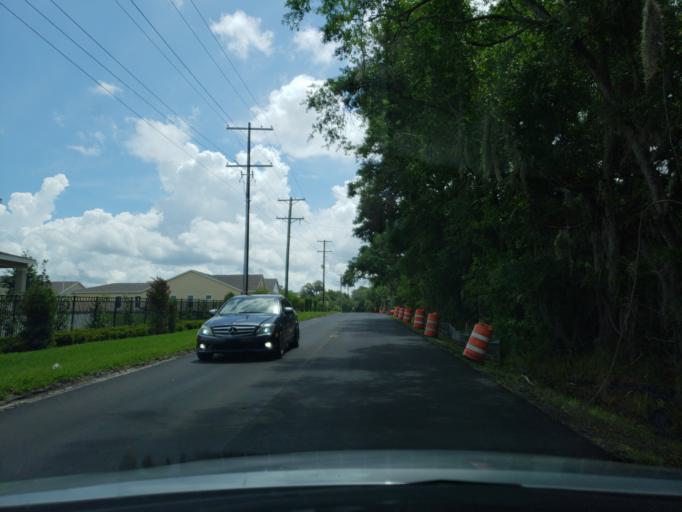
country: US
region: Florida
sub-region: Hillsborough County
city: Riverview
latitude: 27.8864
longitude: -82.3133
